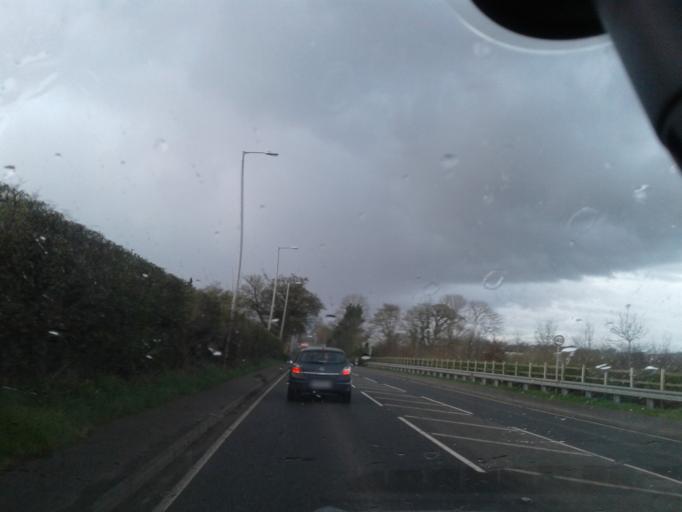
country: GB
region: Northern Ireland
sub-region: Strabane District
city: Sion Mills
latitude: 54.8032
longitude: -7.4731
